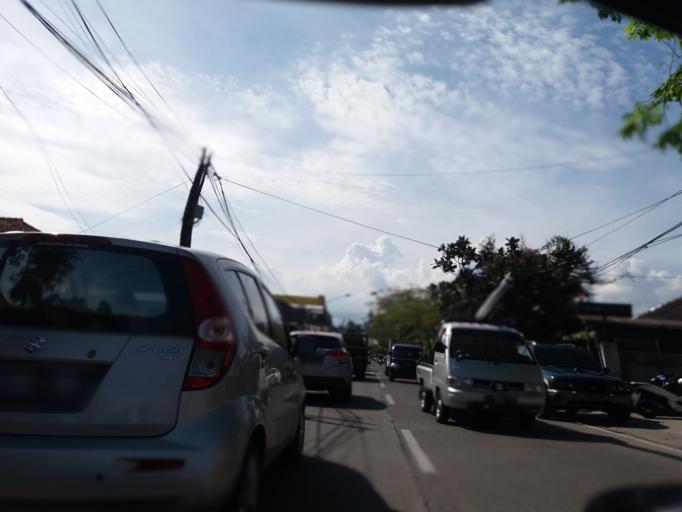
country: ID
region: West Java
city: Bandung
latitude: -6.9407
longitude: 107.6128
